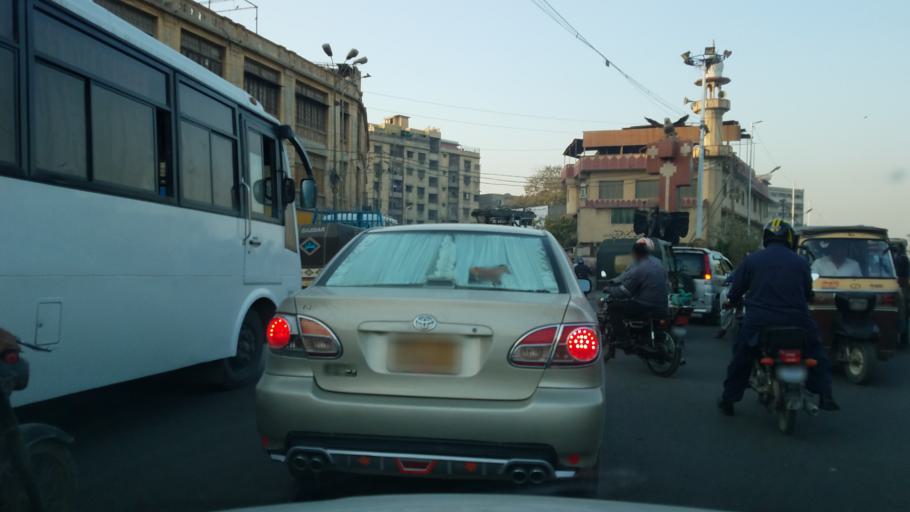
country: PK
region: Sindh
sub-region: Karachi District
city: Karachi
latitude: 24.8758
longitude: 67.0209
